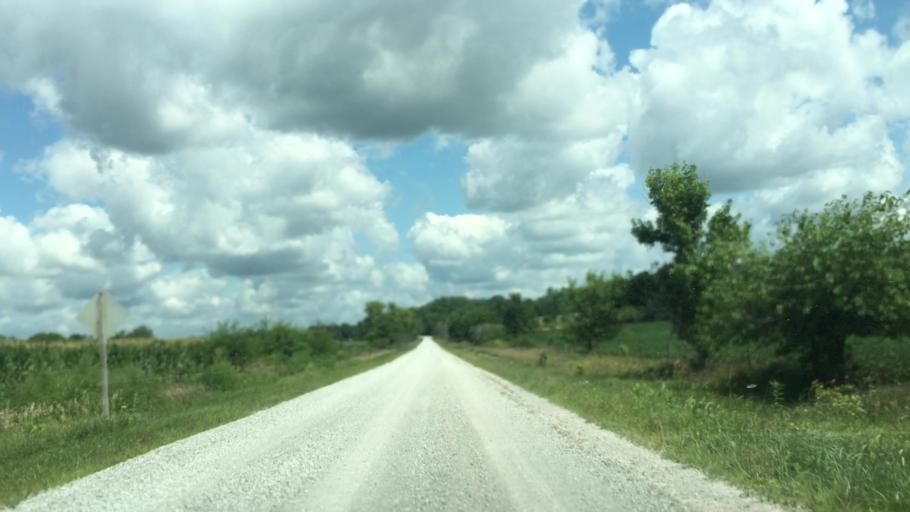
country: US
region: Iowa
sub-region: Linn County
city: Lisbon
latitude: 41.8295
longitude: -91.3906
